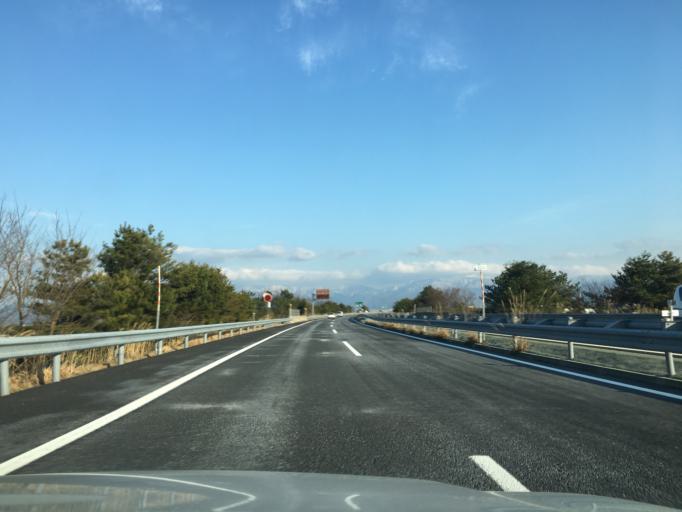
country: JP
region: Yamagata
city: Sagae
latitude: 38.3621
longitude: 140.2849
